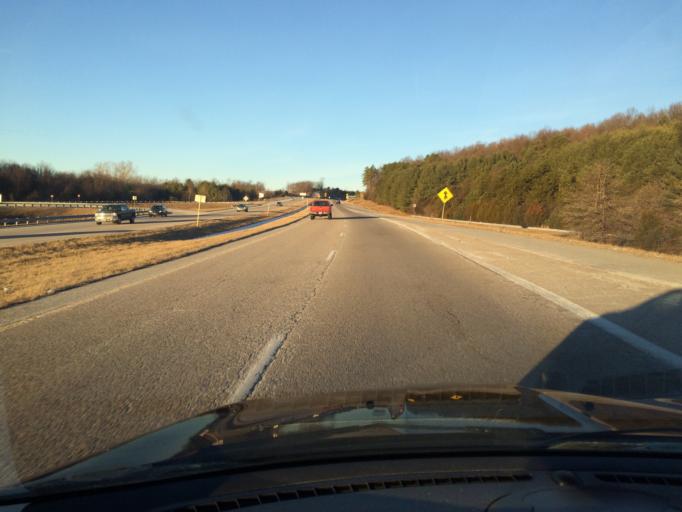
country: US
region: Virginia
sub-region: Augusta County
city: Jolivue
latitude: 38.1262
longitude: -79.0771
